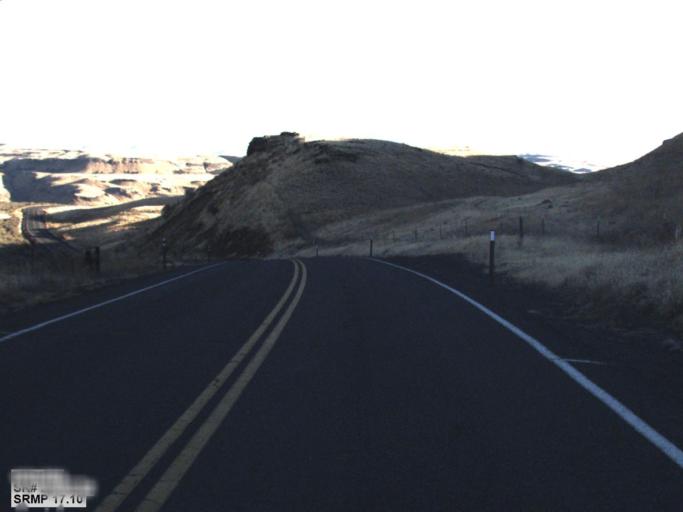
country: US
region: Washington
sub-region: Walla Walla County
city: Waitsburg
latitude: 46.6148
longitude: -118.2298
